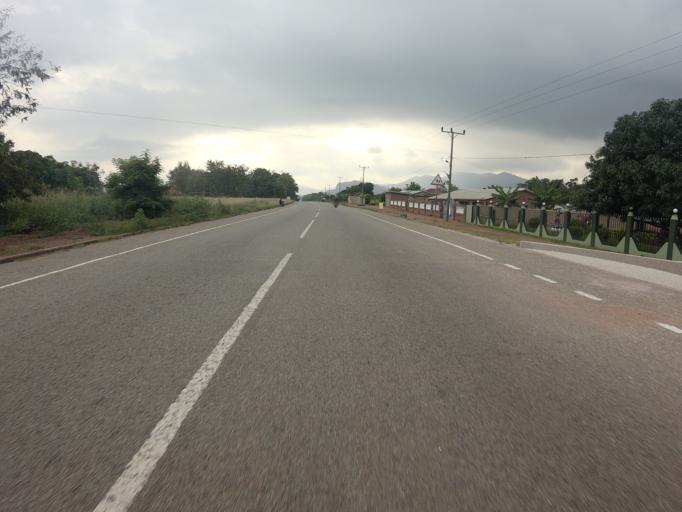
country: GH
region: Volta
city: Ho
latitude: 6.7738
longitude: 0.4782
